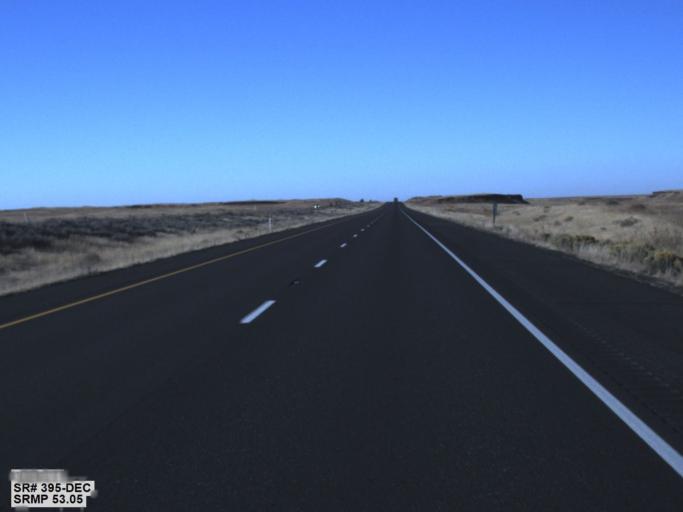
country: US
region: Washington
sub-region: Franklin County
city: Connell
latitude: 46.6327
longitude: -118.8782
